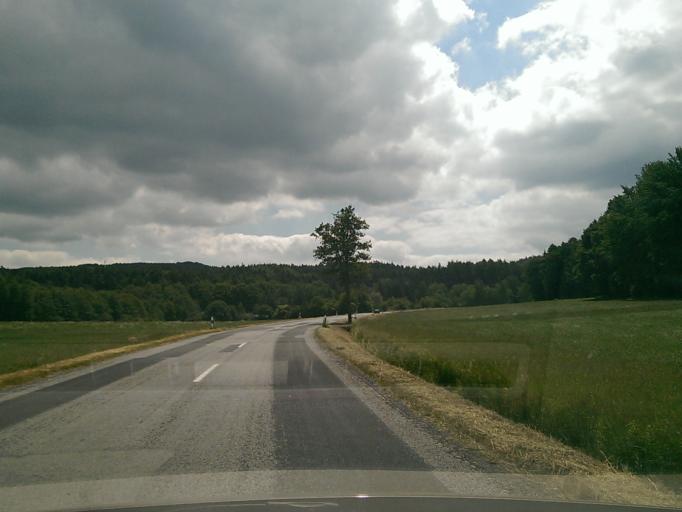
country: DE
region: Saxony
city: Kurort Jonsdorf
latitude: 50.8634
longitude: 14.6931
